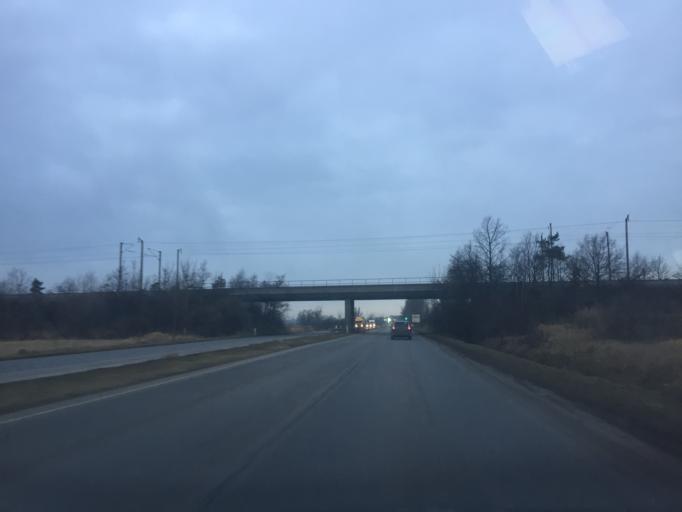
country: DK
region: Zealand
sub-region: Solrod Kommune
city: Solrod Strand
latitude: 55.5132
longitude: 12.2016
